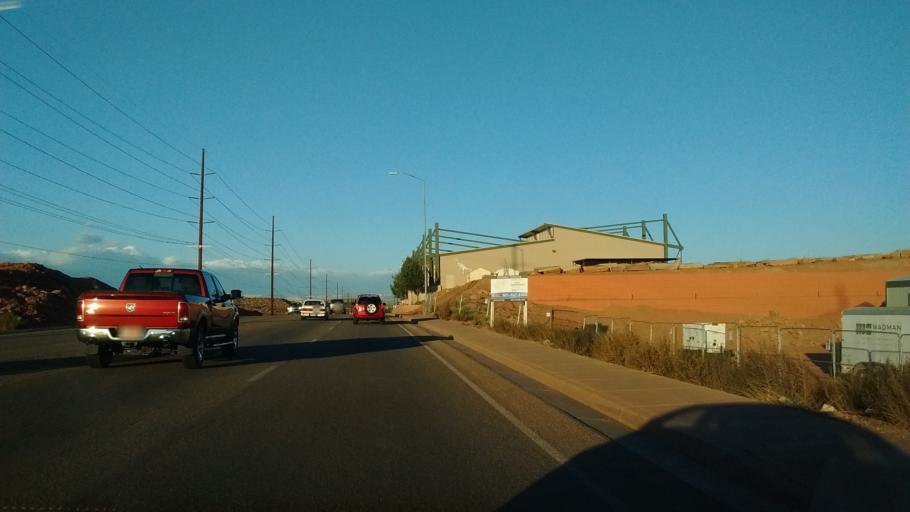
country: US
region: Utah
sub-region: Washington County
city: Washington
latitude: 37.1006
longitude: -113.5362
